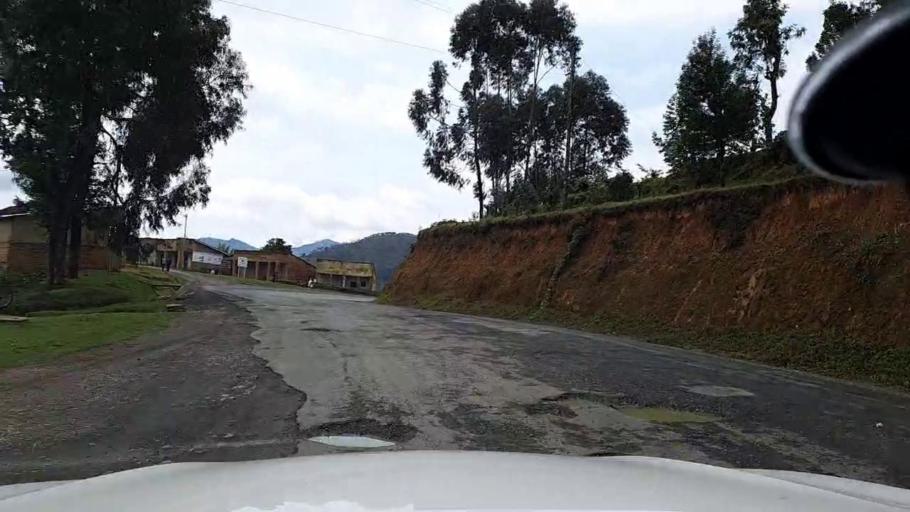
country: RW
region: Western Province
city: Kibuye
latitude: -2.0681
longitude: 29.5395
